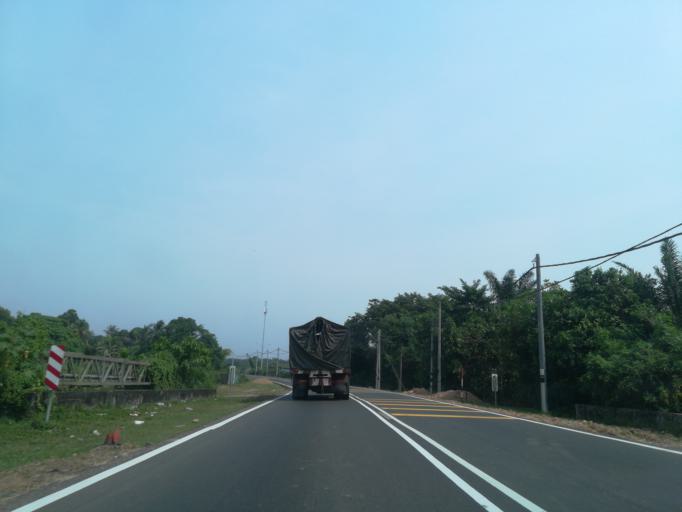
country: MY
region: Penang
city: Tasek Glugor
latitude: 5.4624
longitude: 100.5465
